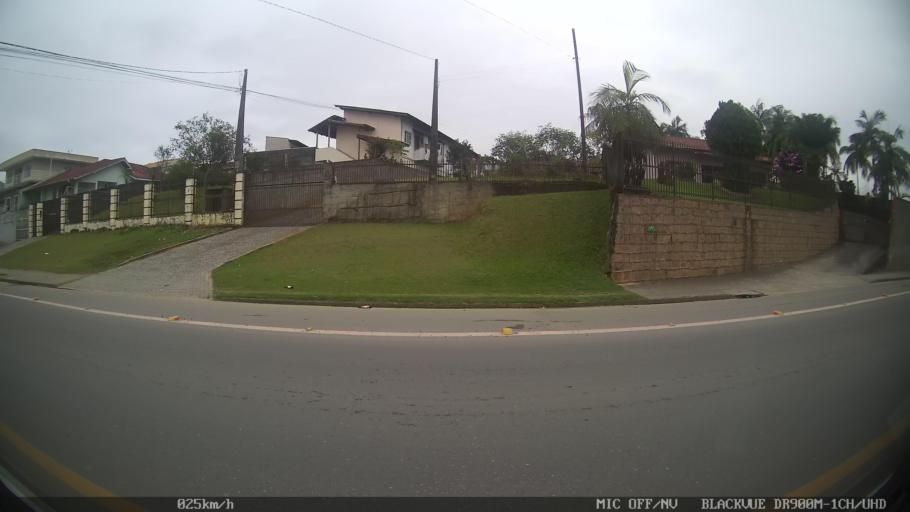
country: BR
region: Santa Catarina
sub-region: Joinville
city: Joinville
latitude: -26.3421
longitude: -48.8166
